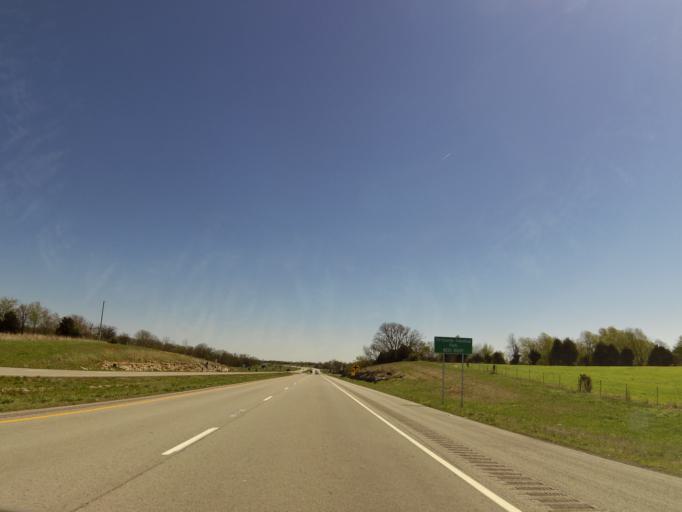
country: US
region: Kentucky
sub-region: Logan County
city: Auburn
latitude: 36.8918
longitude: -86.6212
